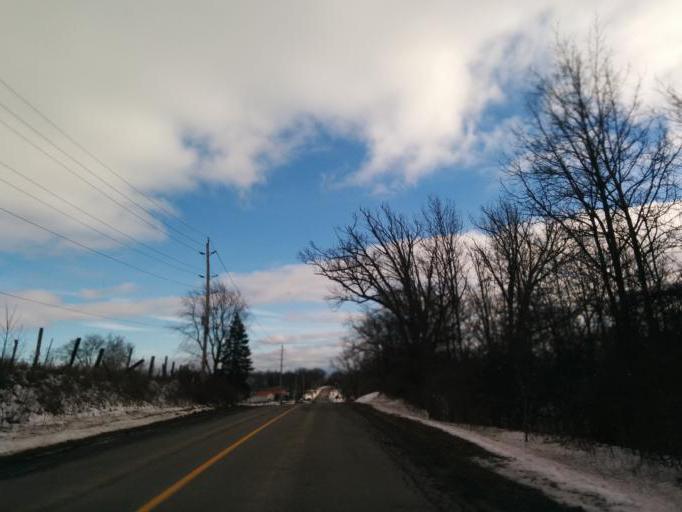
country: CA
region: Ontario
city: Ancaster
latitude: 42.9495
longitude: -79.8720
